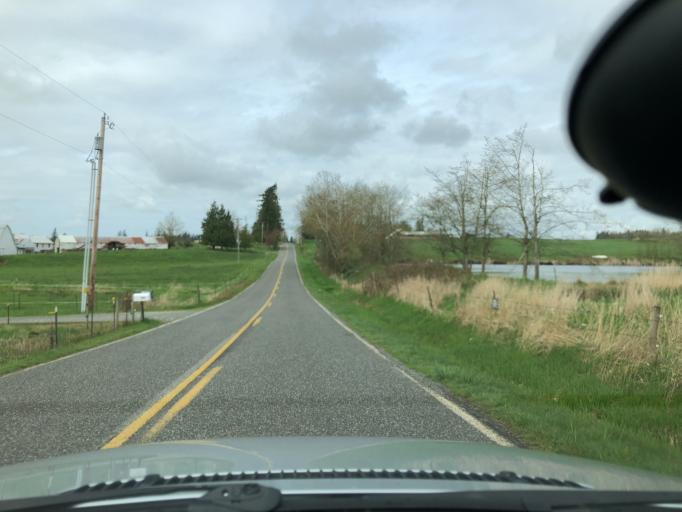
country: US
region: Washington
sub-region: Whatcom County
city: Lynden
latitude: 48.9831
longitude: -122.5373
